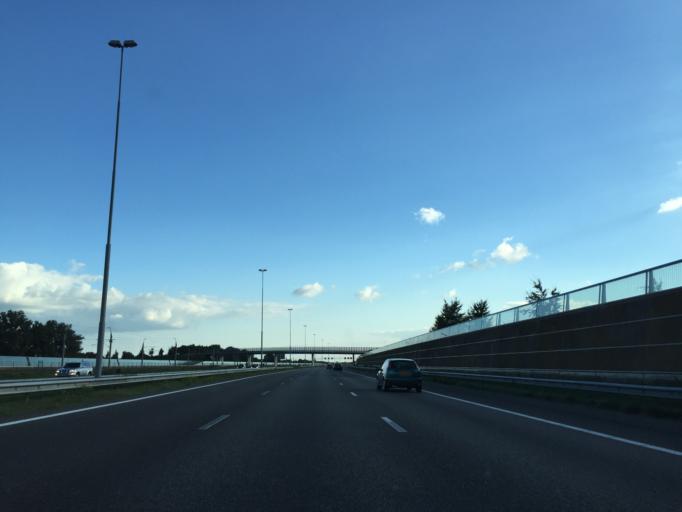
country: NL
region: North Brabant
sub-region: Gemeente Breda
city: Breda
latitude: 51.5505
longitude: 4.7392
